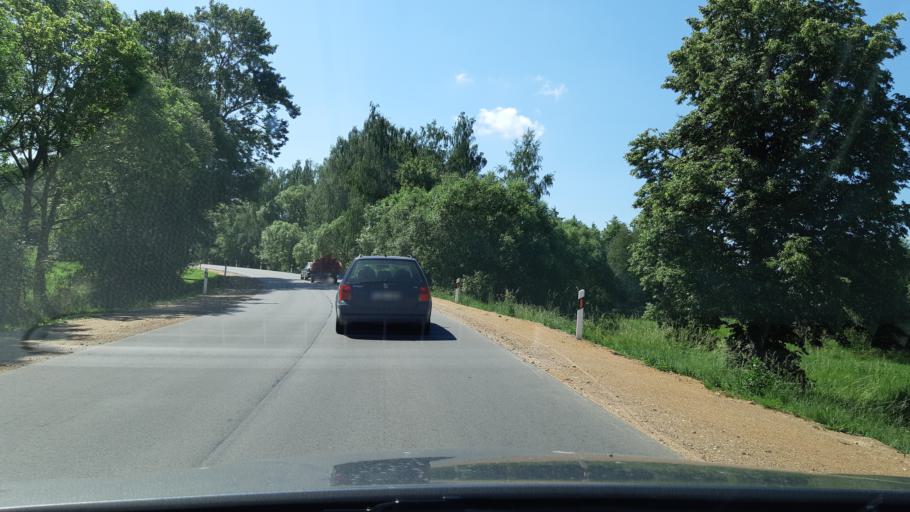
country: LT
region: Kauno apskritis
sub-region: Kauno rajonas
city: Karmelava
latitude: 54.8423
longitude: 24.2355
